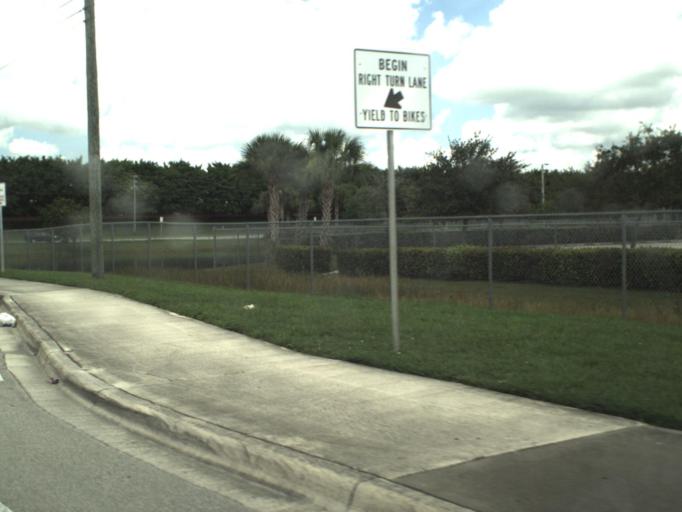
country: US
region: Florida
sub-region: Palm Beach County
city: Lake Belvedere Estates
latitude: 26.6510
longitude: -80.1804
